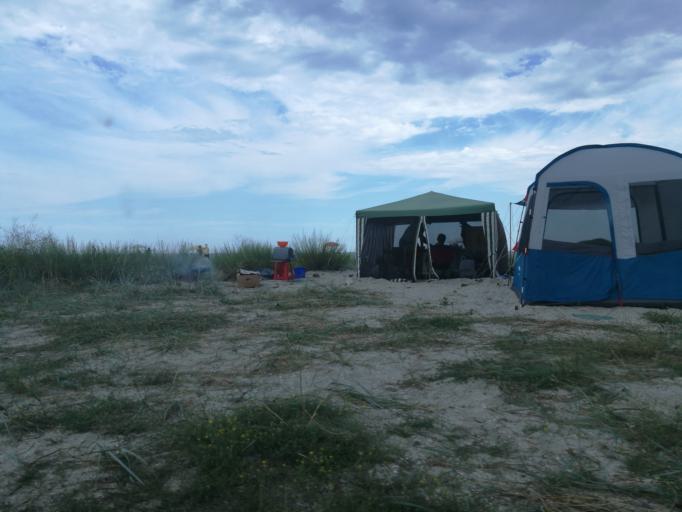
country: RO
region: Constanta
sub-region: Comuna Corbu
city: Corbu
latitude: 44.4295
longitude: 28.7667
